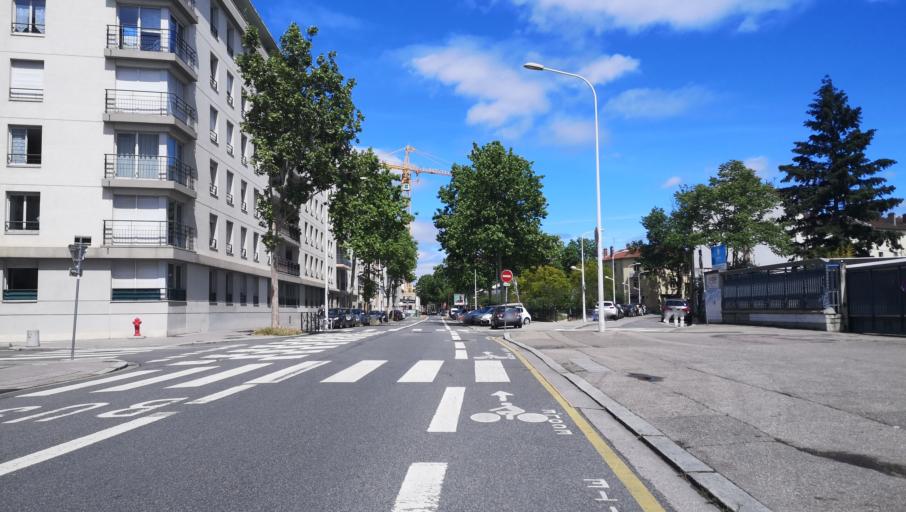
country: FR
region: Rhone-Alpes
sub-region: Departement du Rhone
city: Lyon
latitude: 45.7401
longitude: 4.8676
